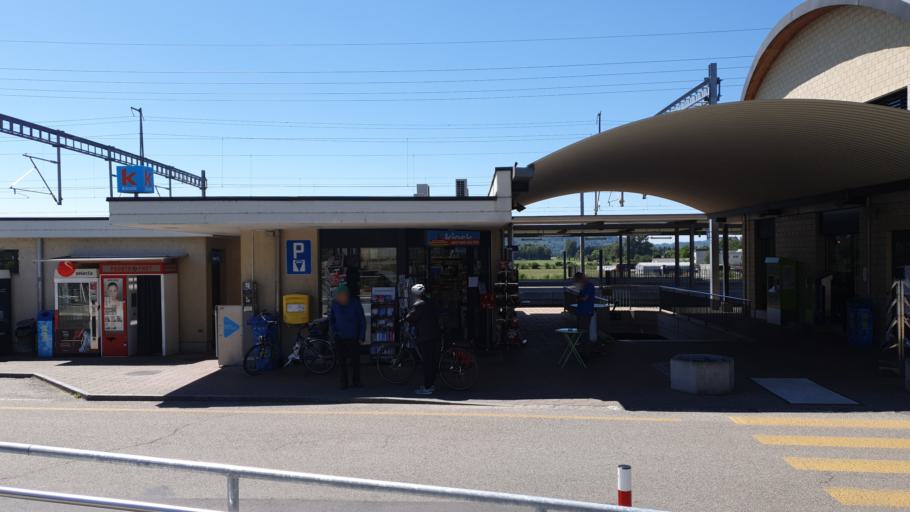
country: CH
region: Bern
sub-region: Seeland District
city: Ins
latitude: 47.0000
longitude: 7.0998
